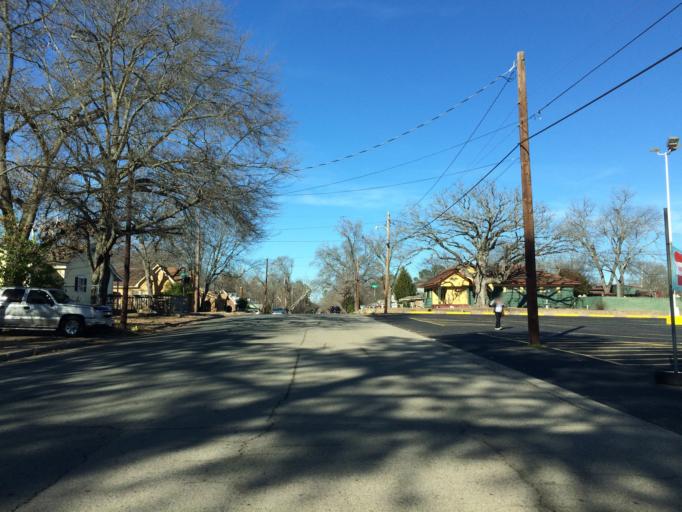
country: US
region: Texas
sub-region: Wood County
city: Mineola
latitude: 32.6678
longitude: -95.4855
